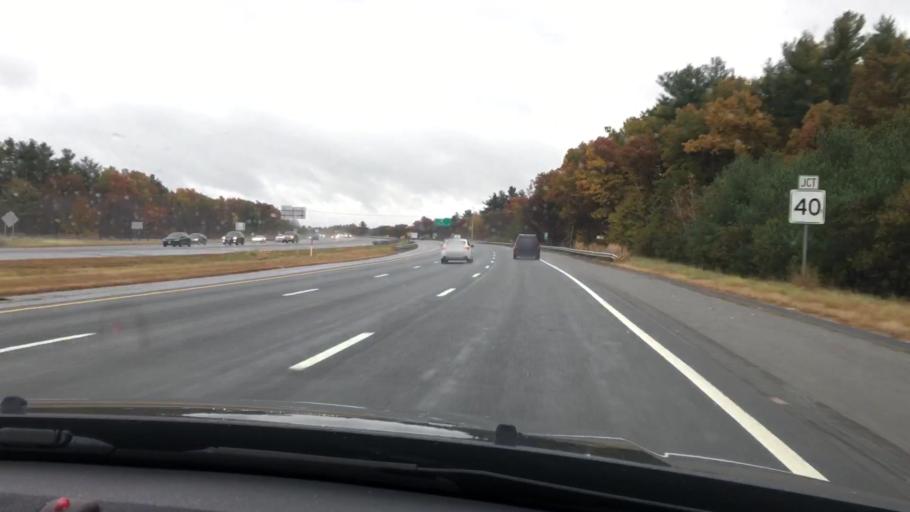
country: US
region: Massachusetts
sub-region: Middlesex County
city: Tyngsboro
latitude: 42.6339
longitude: -71.4079
